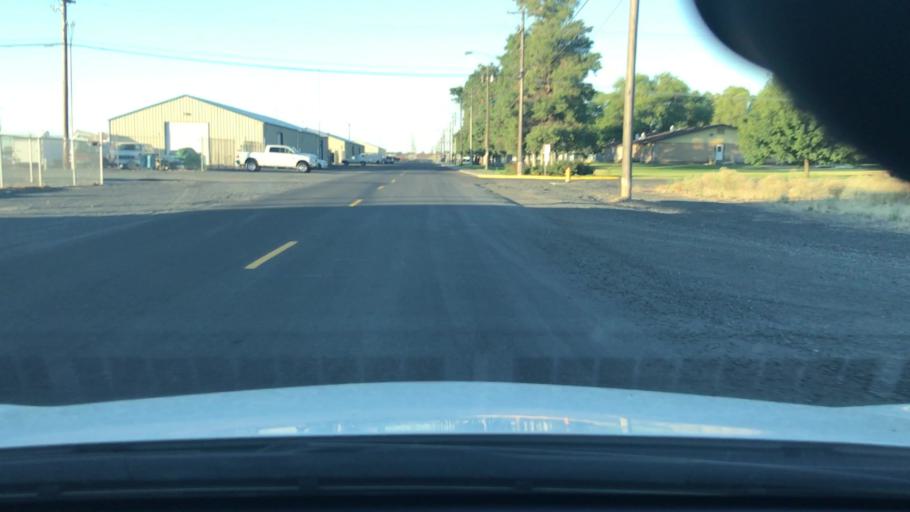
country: US
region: Washington
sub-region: Grant County
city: Moses Lake North
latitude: 47.1865
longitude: -119.3166
